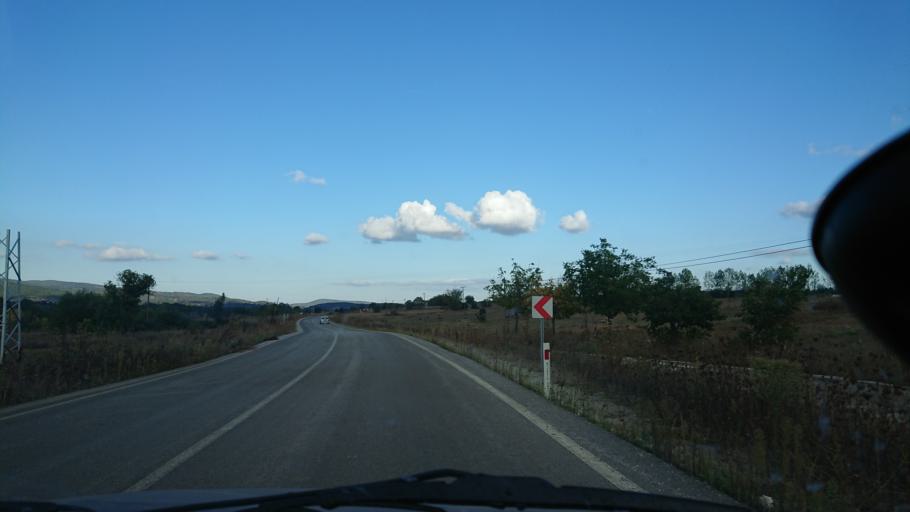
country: TR
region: Bilecik
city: Pazaryeri
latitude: 40.0112
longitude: 29.8154
